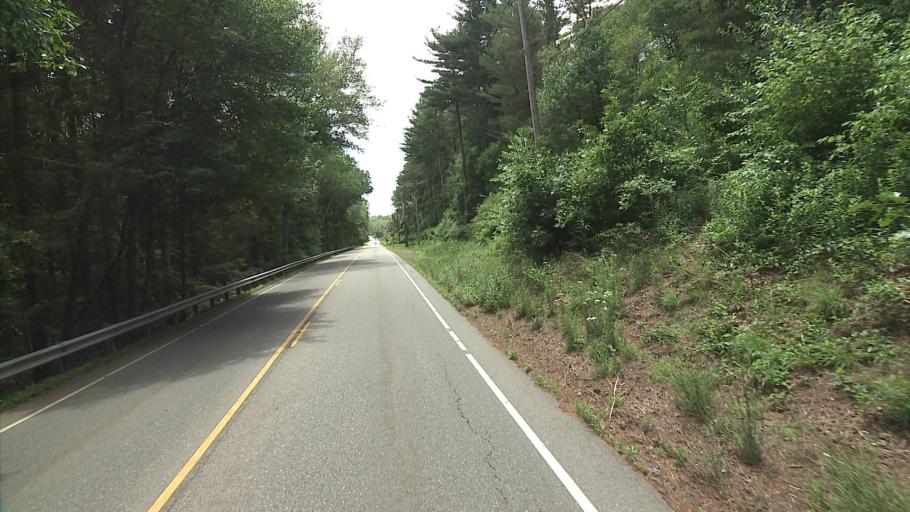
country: US
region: Connecticut
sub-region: New London County
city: Preston City
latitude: 41.5090
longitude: -71.9834
